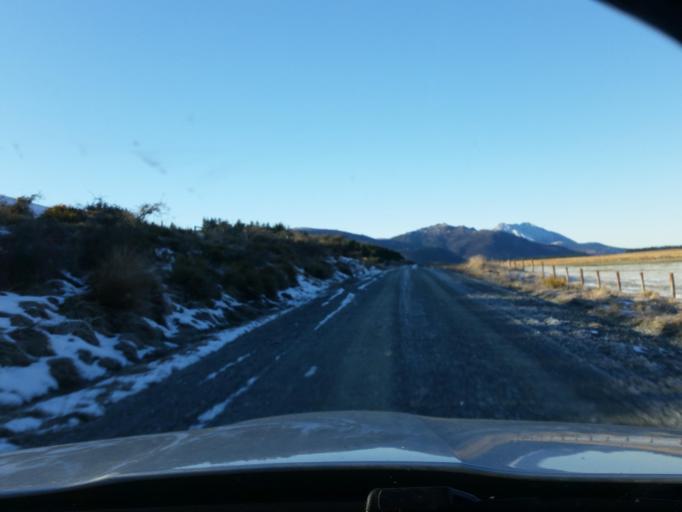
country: NZ
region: Southland
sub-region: Southland District
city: Te Anau
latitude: -45.4723
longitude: 168.0922
